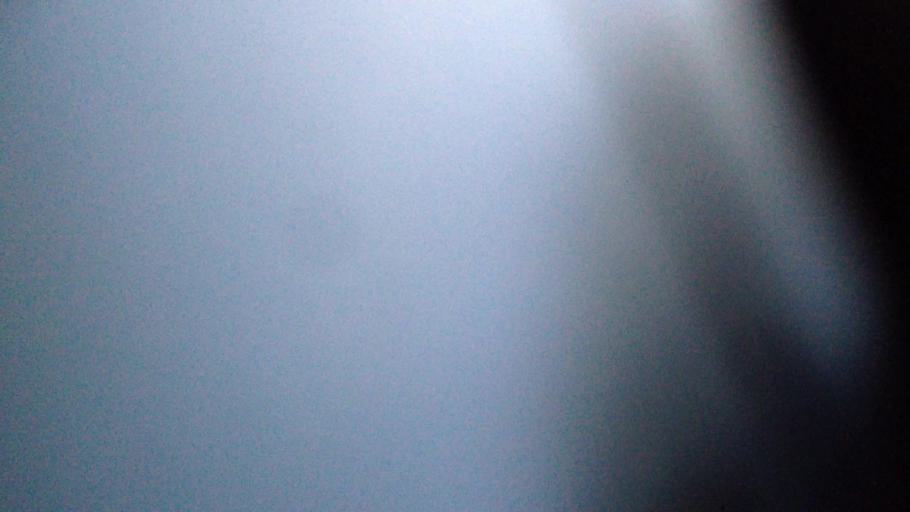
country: US
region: New York
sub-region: Greene County
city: Catskill
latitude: 42.2168
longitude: -73.8323
